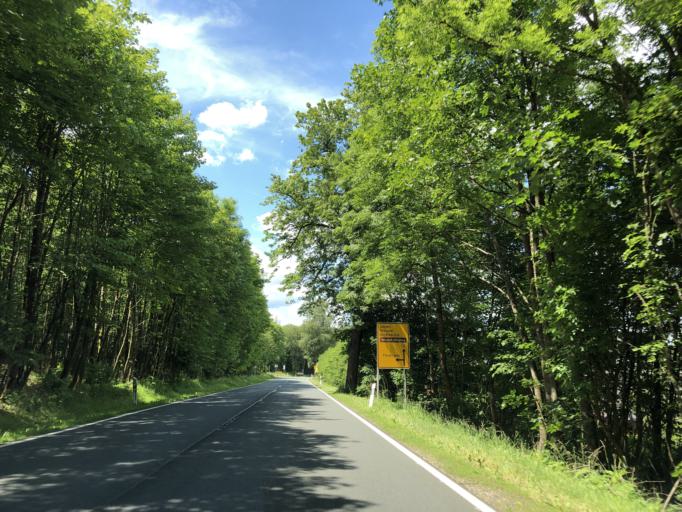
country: DE
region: North Rhine-Westphalia
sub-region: Regierungsbezirk Arnsberg
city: Erndtebruck
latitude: 50.9877
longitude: 8.3132
